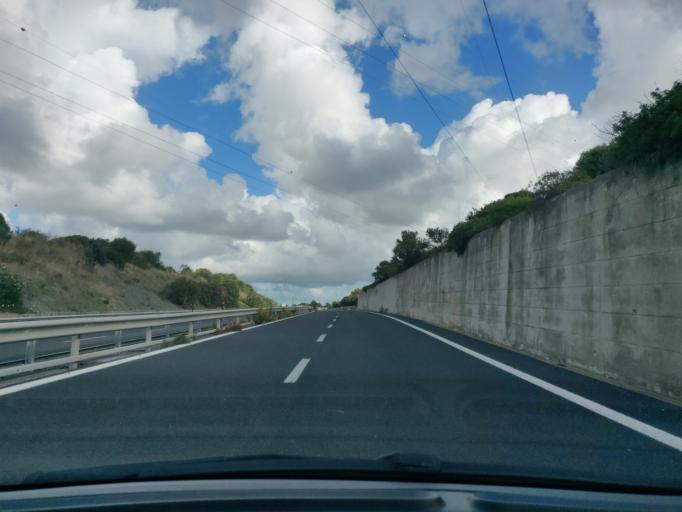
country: IT
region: Latium
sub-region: Citta metropolitana di Roma Capitale
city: Civitavecchia
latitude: 42.1134
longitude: 11.7925
